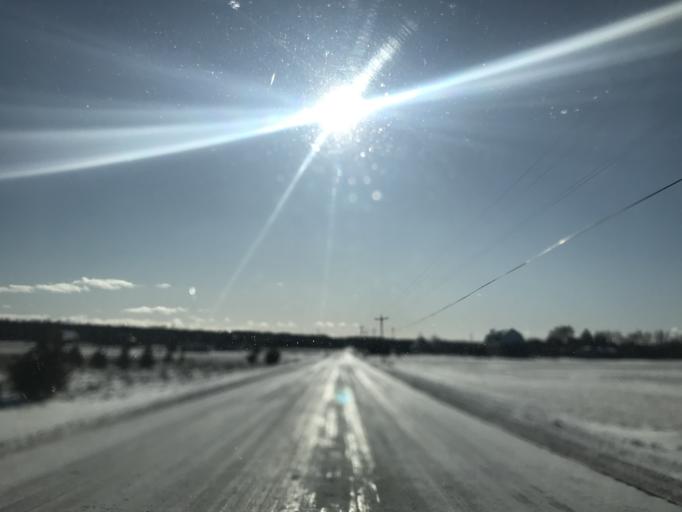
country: US
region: Wisconsin
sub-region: Door County
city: Sturgeon Bay
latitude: 44.8375
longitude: -87.5040
